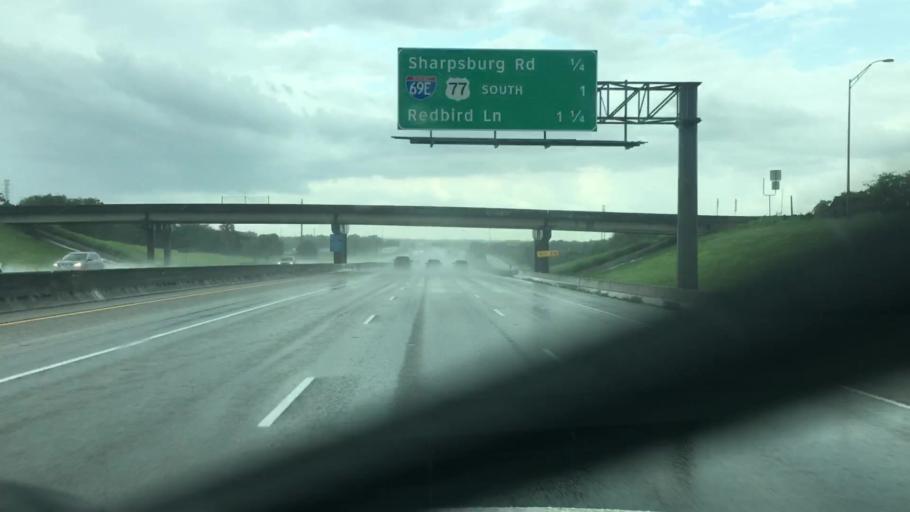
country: US
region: Texas
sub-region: Nueces County
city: Robstown
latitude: 27.8567
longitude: -97.6010
